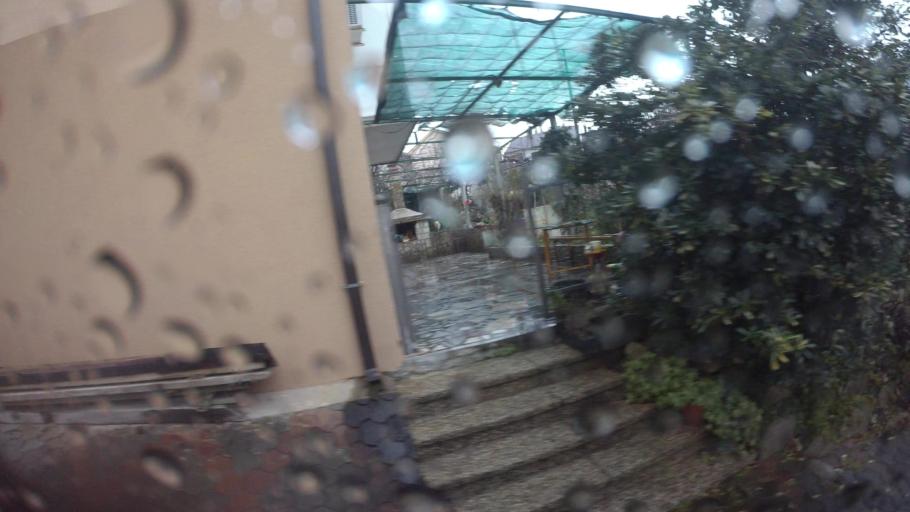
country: BA
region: Federation of Bosnia and Herzegovina
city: Cim
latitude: 43.3470
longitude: 17.7863
